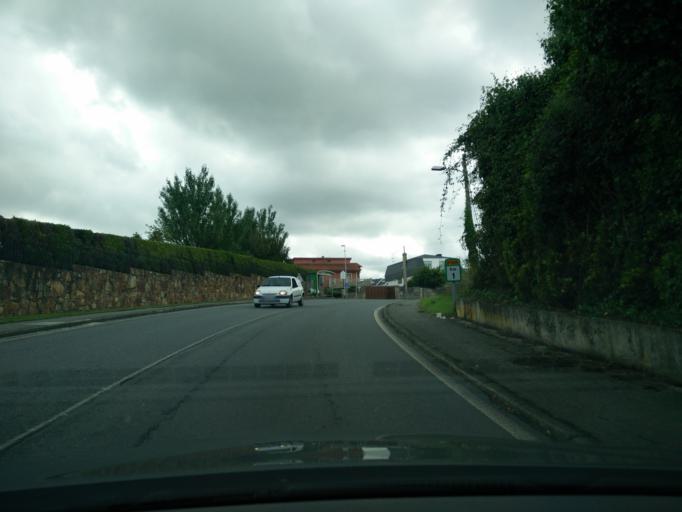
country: ES
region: Galicia
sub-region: Provincia da Coruna
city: Culleredo
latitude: 43.3268
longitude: -8.4032
